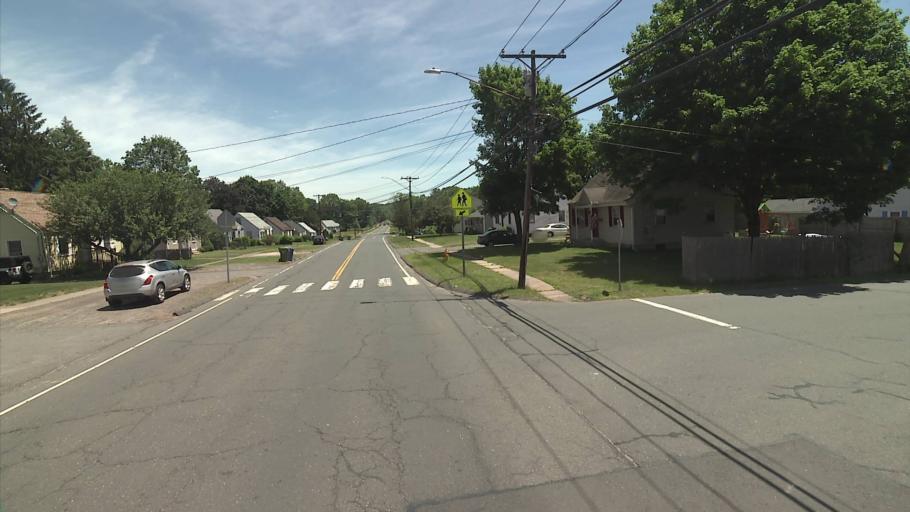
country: US
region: Connecticut
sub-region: Hartford County
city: Plainville
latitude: 41.5962
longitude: -72.8651
